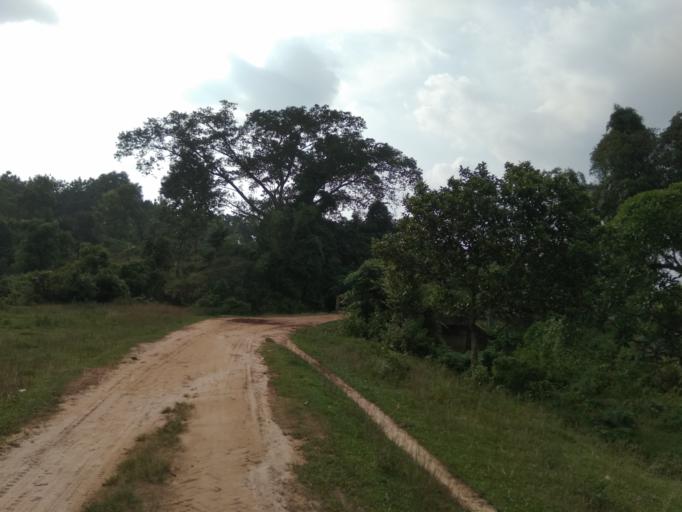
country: BD
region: Chittagong
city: Manikchari
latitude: 22.9319
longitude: 91.9108
